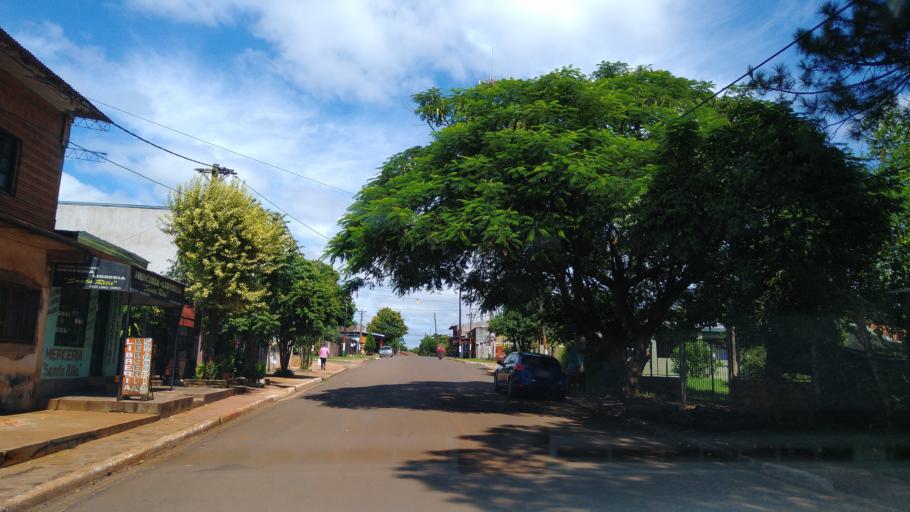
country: AR
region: Misiones
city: Garupa
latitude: -27.4566
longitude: -55.8590
